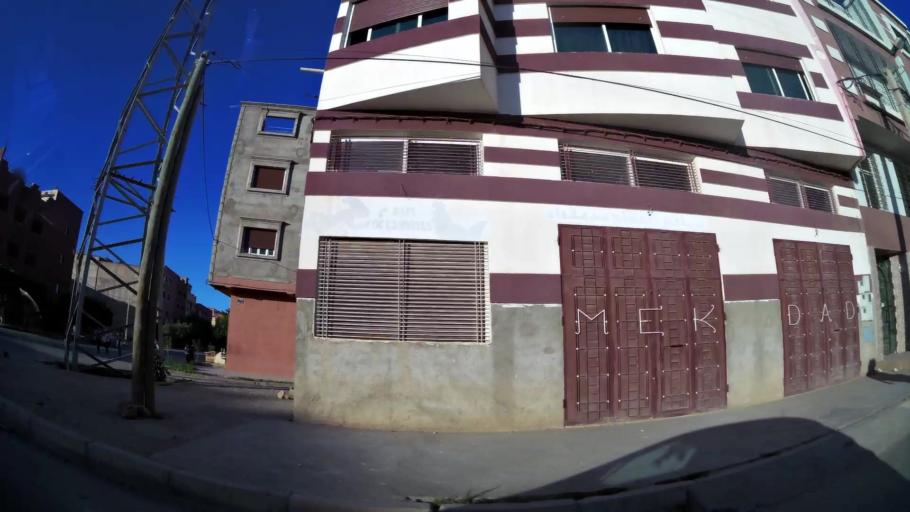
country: MA
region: Oriental
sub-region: Berkane-Taourirt
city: Berkane
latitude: 34.9220
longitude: -2.3117
